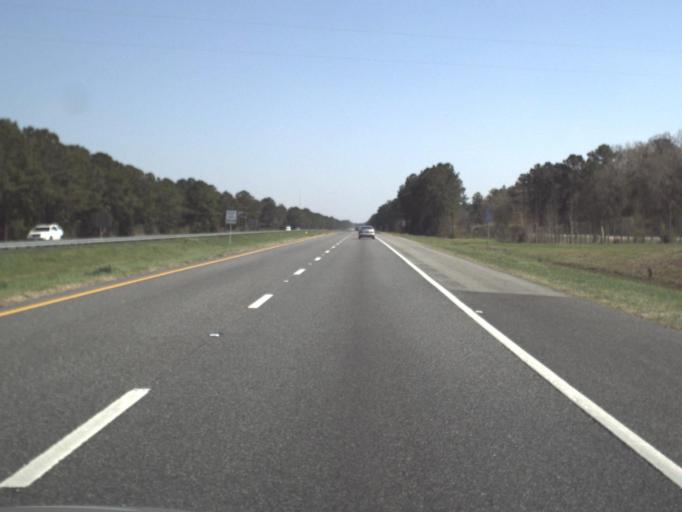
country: US
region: Florida
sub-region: Jackson County
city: Marianna
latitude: 30.7496
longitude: -85.2654
